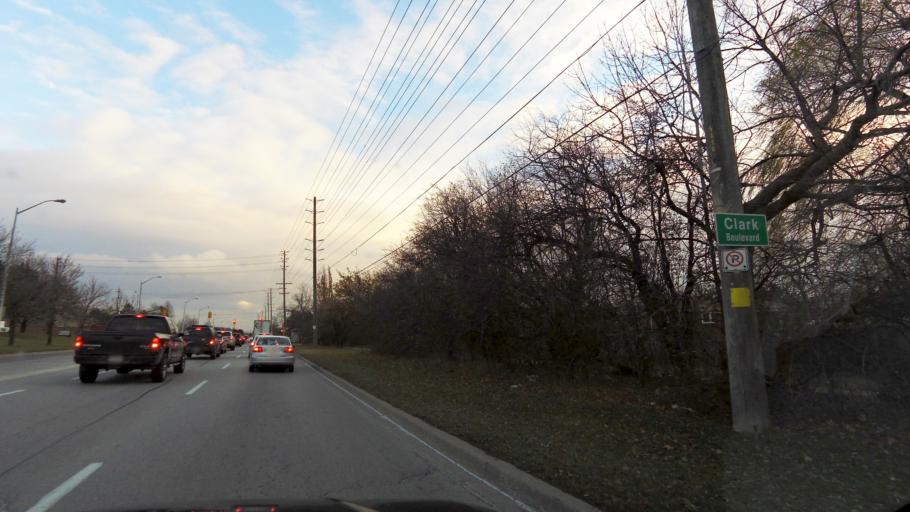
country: CA
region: Ontario
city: Brampton
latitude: 43.7281
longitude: -79.6988
